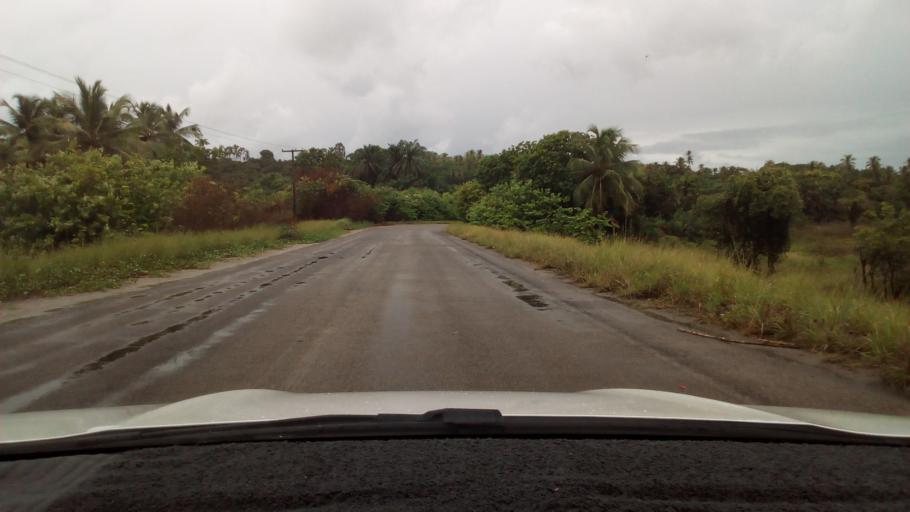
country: BR
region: Paraiba
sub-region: Pitimbu
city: Pitimbu
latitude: -7.4447
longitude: -34.8345
